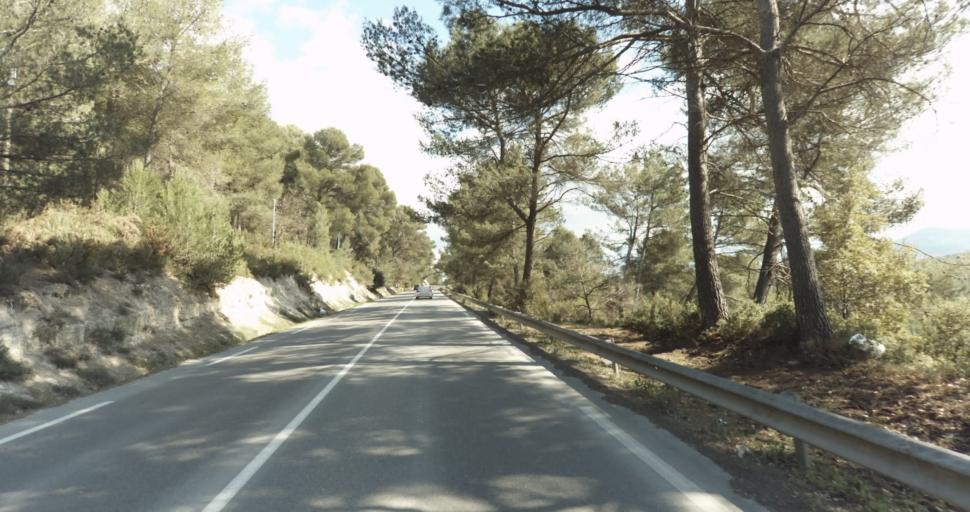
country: FR
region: Provence-Alpes-Cote d'Azur
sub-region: Departement des Bouches-du-Rhone
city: Gardanne
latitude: 43.4507
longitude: 5.4997
